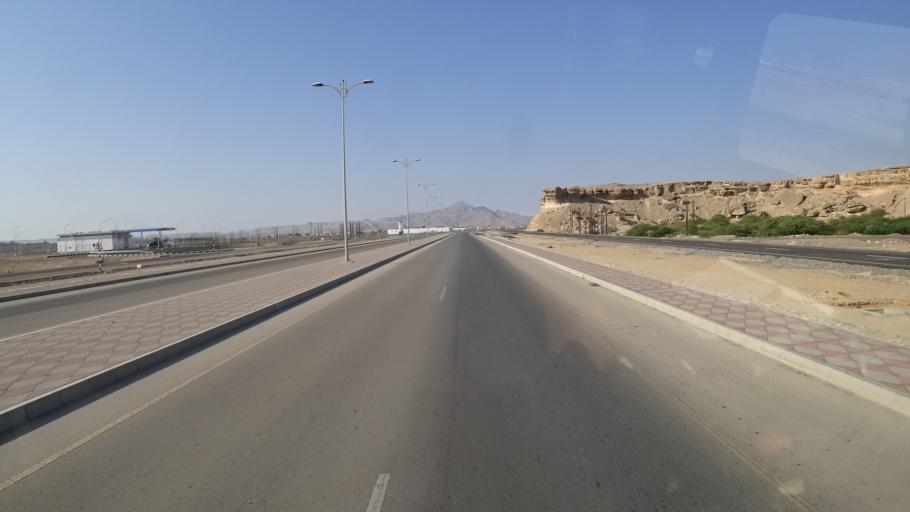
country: OM
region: Ash Sharqiyah
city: Sur
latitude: 22.5937
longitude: 59.4786
